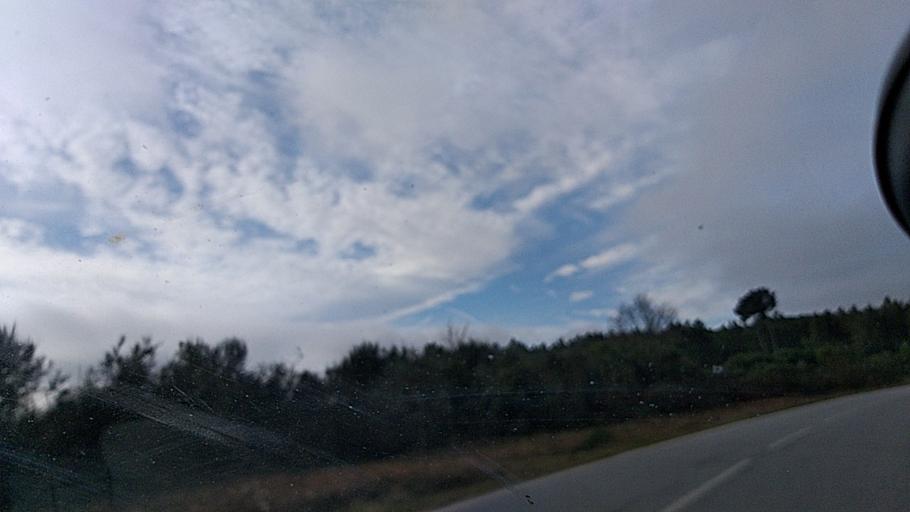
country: PT
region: Guarda
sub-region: Aguiar da Beira
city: Aguiar da Beira
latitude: 40.7745
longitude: -7.5197
